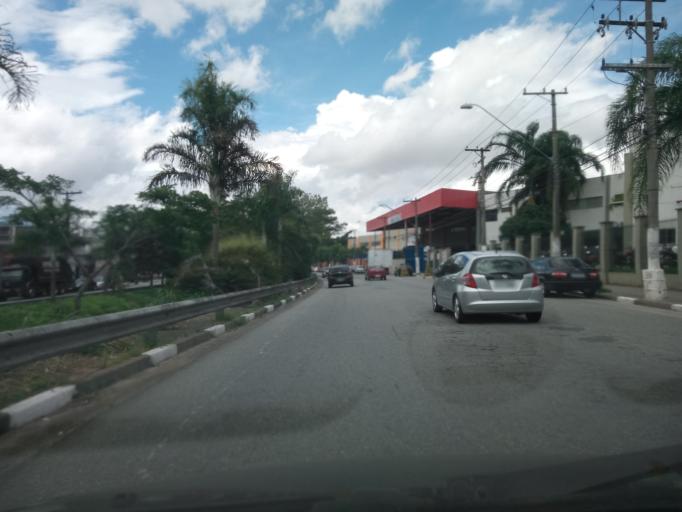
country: BR
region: Sao Paulo
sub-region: Sao Bernardo Do Campo
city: Sao Bernardo do Campo
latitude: -23.6940
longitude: -46.5799
